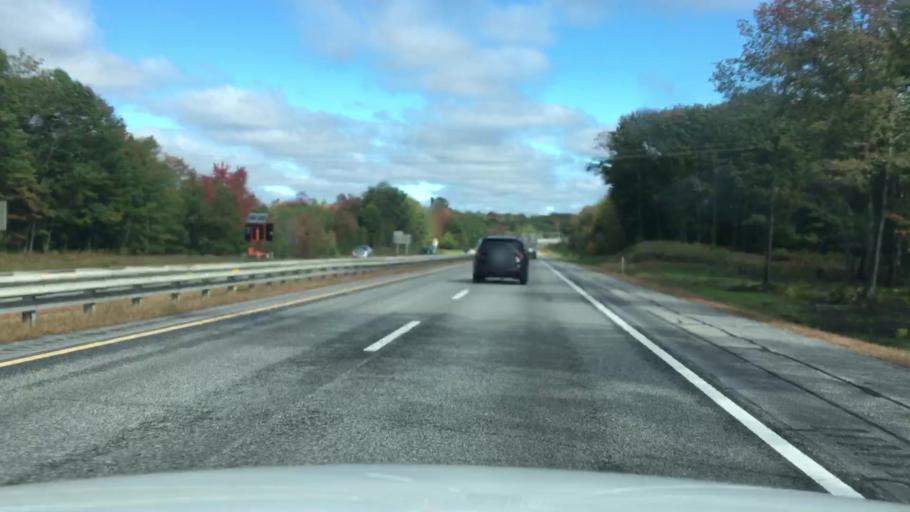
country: US
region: Maine
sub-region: Cumberland County
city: Freeport
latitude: 43.8561
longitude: -70.1126
